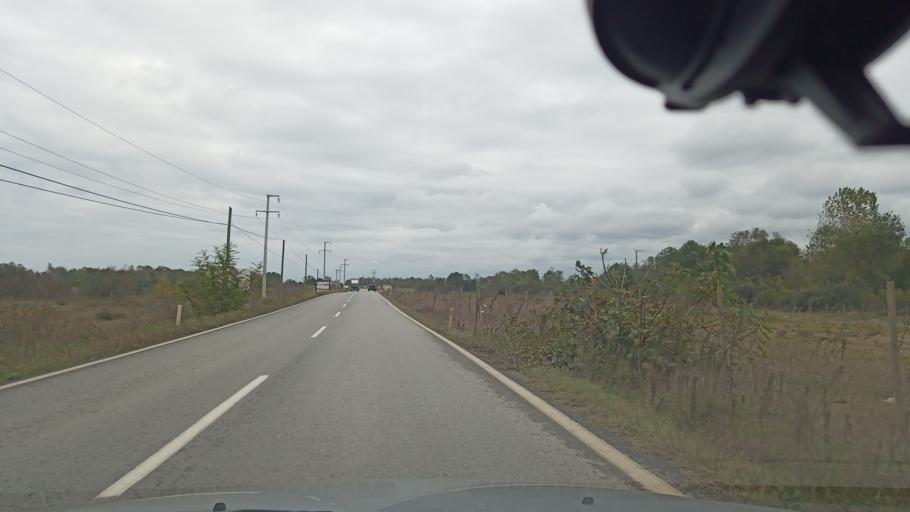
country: TR
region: Sakarya
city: Karasu
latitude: 41.1199
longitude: 30.6009
